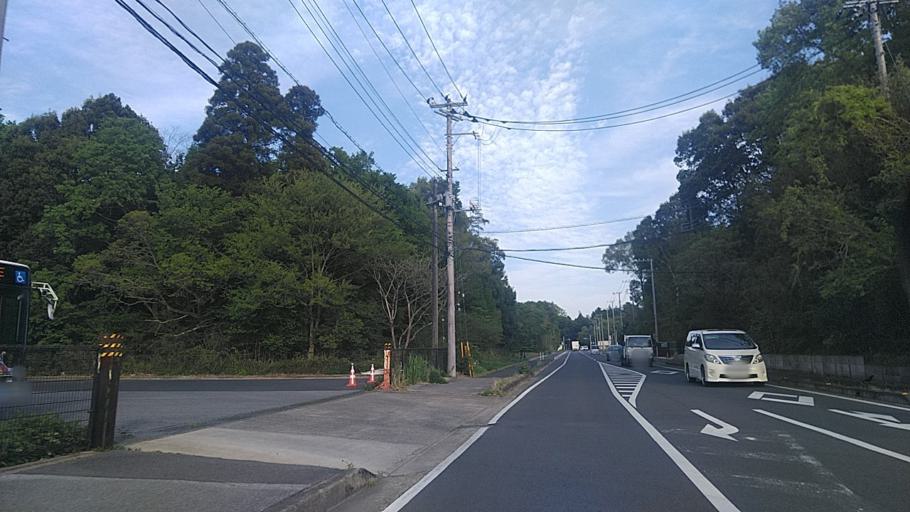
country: JP
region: Chiba
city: Shiroi
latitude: 35.7912
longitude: 140.1453
